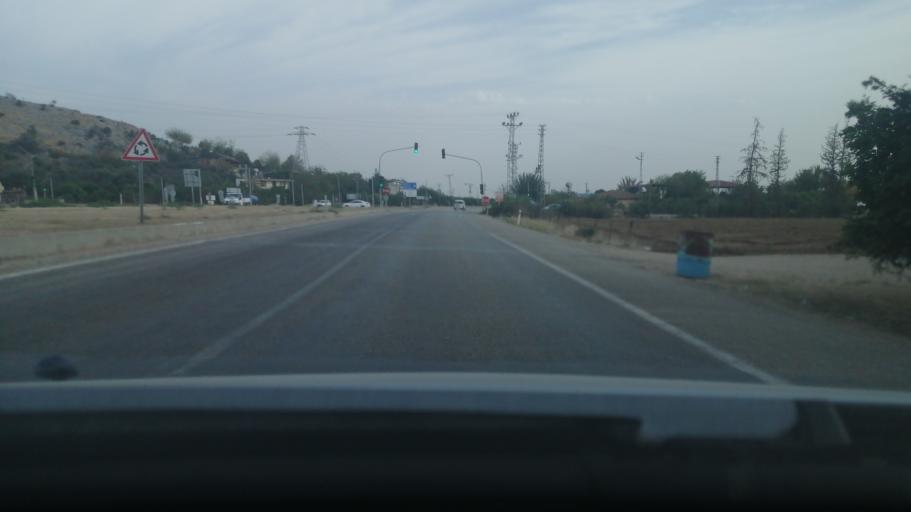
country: TR
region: Adana
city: Kozan
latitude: 37.3803
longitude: 35.8253
